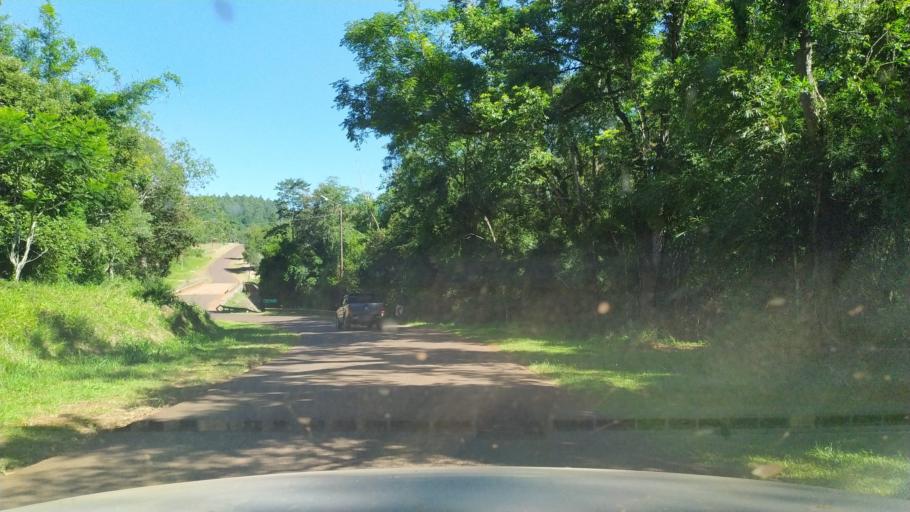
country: AR
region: Misiones
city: Caraguatay
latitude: -26.6543
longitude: -54.7410
